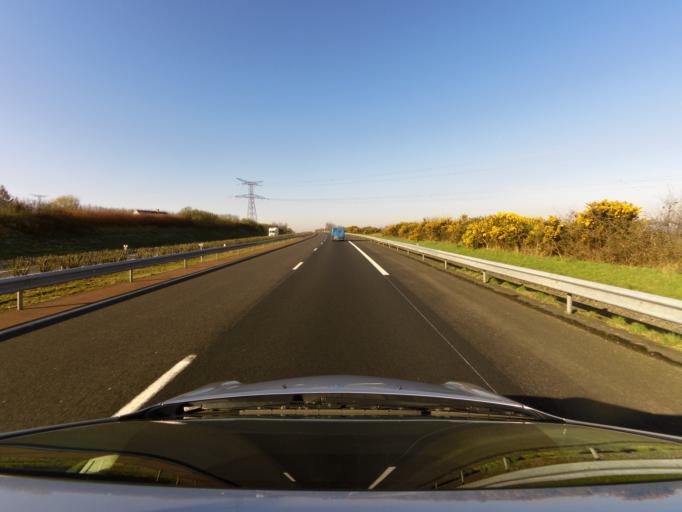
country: FR
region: Lower Normandy
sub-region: Departement de la Manche
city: Percy
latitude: 48.8933
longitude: -1.1295
